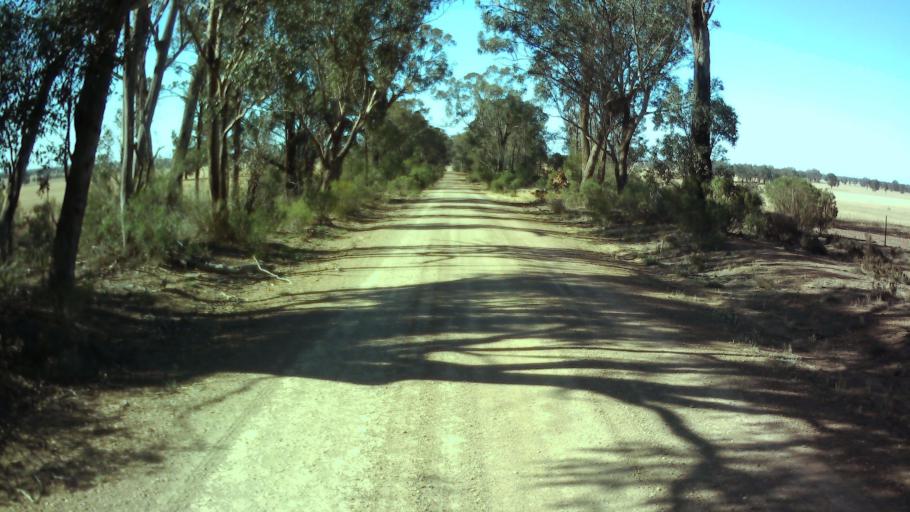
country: AU
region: New South Wales
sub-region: Weddin
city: Grenfell
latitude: -33.9100
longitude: 147.8769
